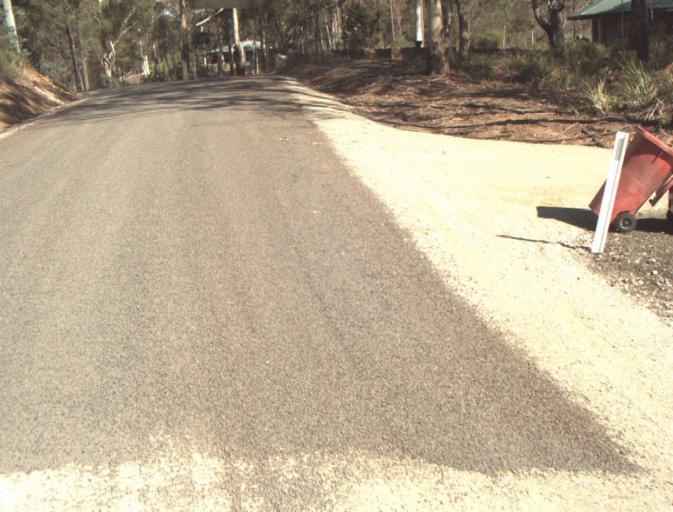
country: AU
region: Tasmania
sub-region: Launceston
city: Mayfield
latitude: -41.2761
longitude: 147.1086
